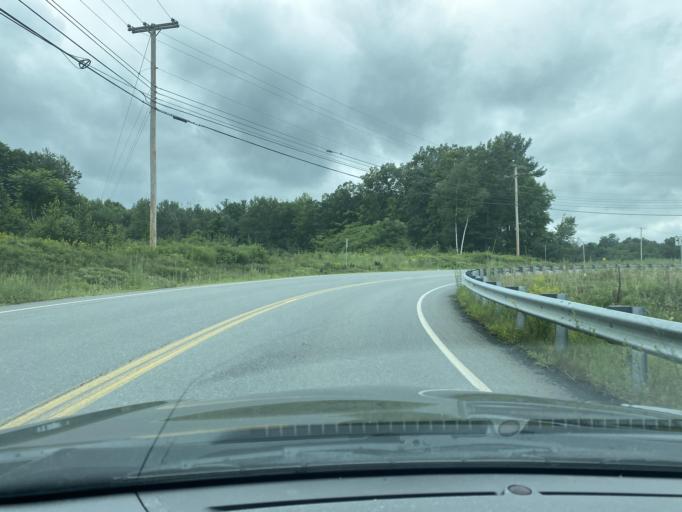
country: US
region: New Hampshire
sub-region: Rockingham County
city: Windham
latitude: 42.8065
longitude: -71.2860
